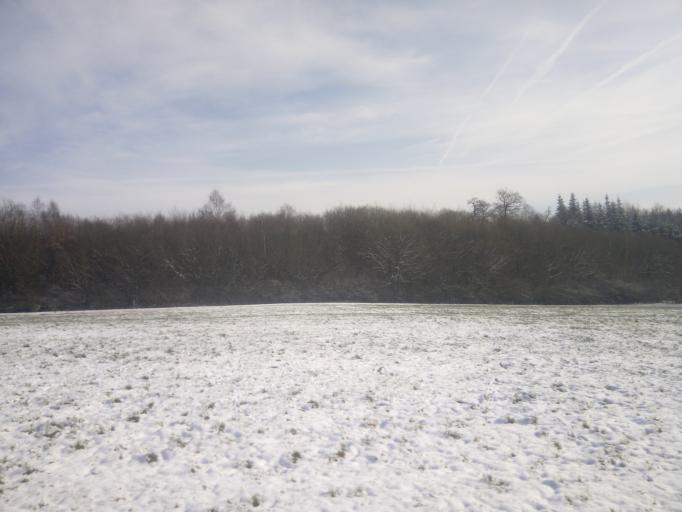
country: LU
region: Grevenmacher
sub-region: Canton d'Echternach
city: Consdorf
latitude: 49.7625
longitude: 6.3368
